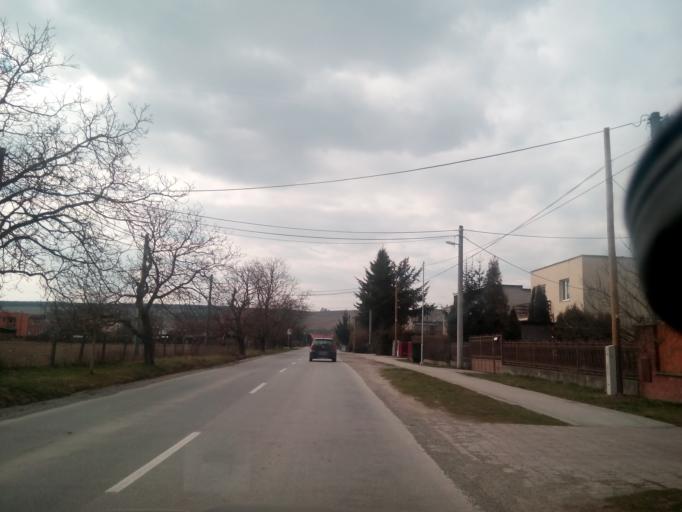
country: SK
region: Kosicky
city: Kosice
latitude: 48.7059
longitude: 21.3376
